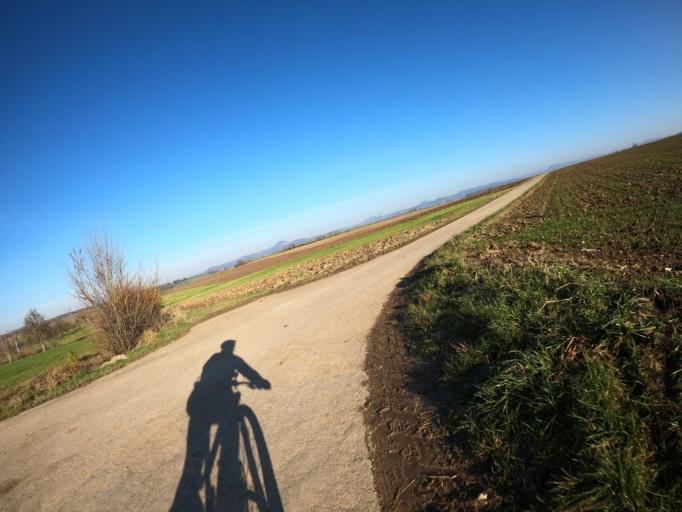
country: DE
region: Baden-Wuerttemberg
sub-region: Regierungsbezirk Stuttgart
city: Heiningen
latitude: 48.6667
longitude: 9.6630
